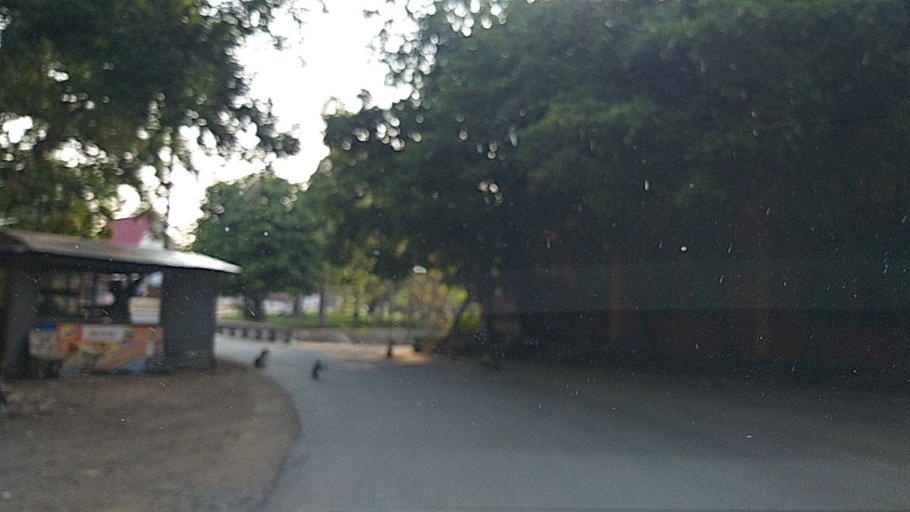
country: TH
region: Sara Buri
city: Saraburi
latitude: 14.4590
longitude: 100.9492
